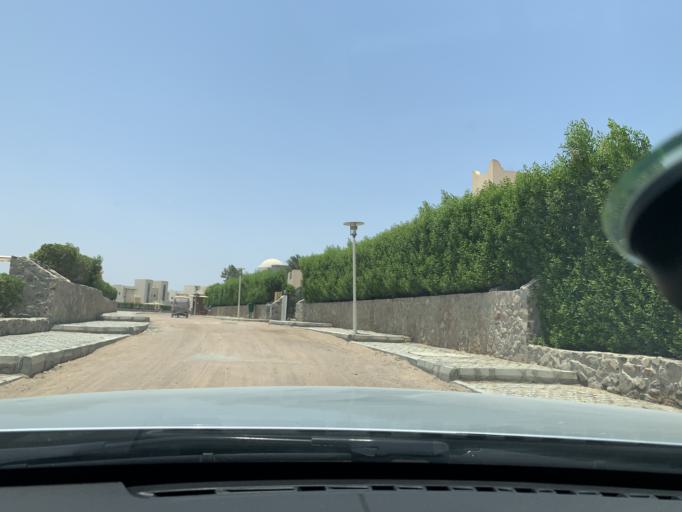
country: EG
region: Red Sea
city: El Gouna
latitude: 27.4147
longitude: 33.6689
